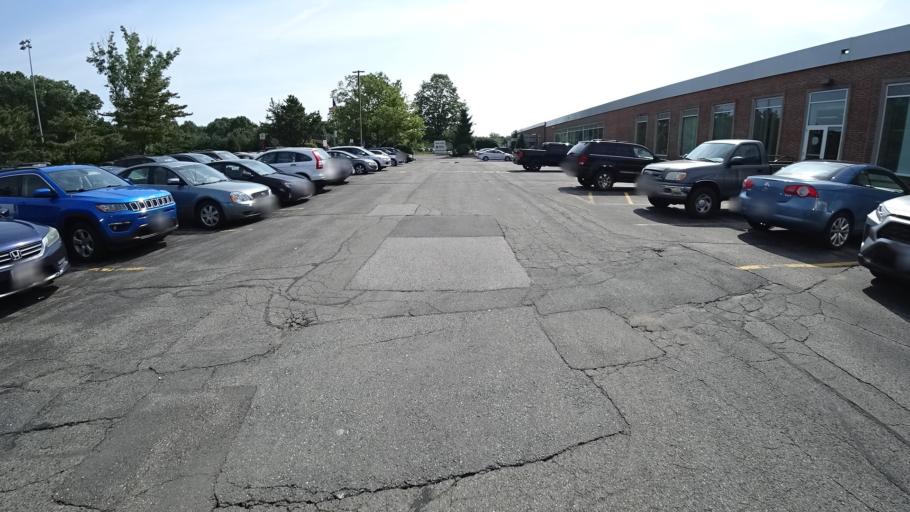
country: US
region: Massachusetts
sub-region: Norfolk County
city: Dedham
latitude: 42.2323
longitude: -71.1696
